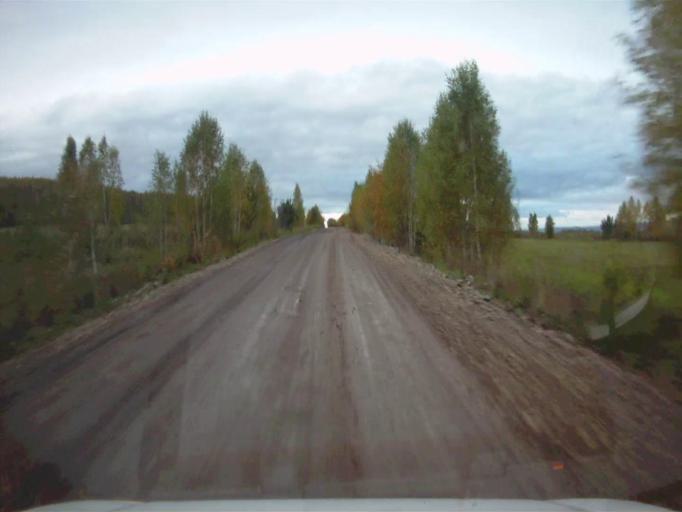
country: RU
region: Sverdlovsk
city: Mikhaylovsk
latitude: 56.1973
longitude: 59.1995
